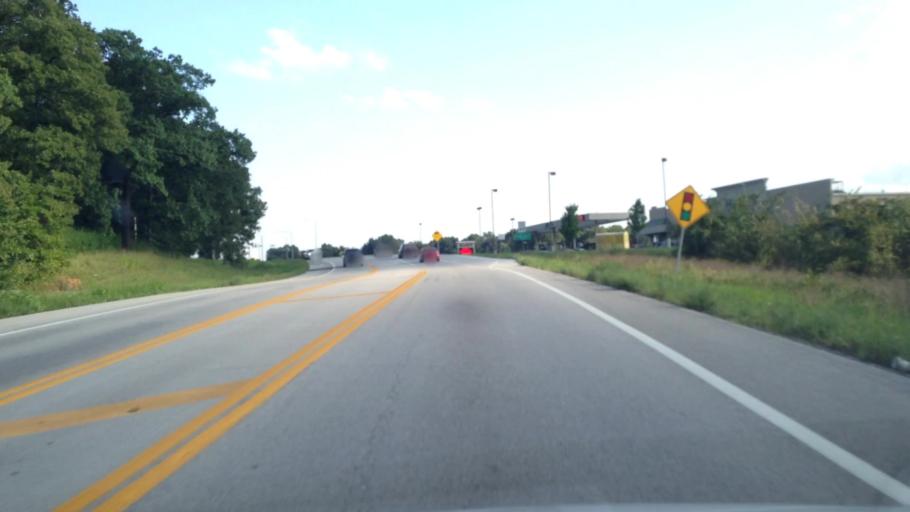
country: US
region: Missouri
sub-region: Jasper County
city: Carl Junction
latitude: 37.1466
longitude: -94.5233
